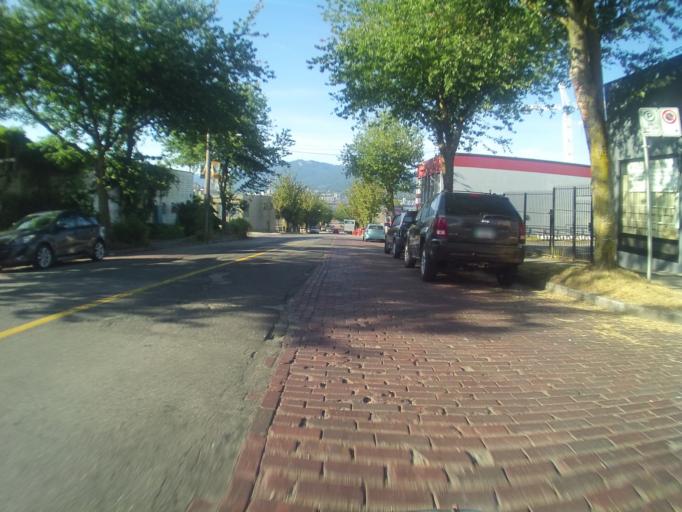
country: CA
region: British Columbia
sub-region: Fraser Valley Regional District
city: North Vancouver
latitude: 49.2818
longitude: -123.0655
